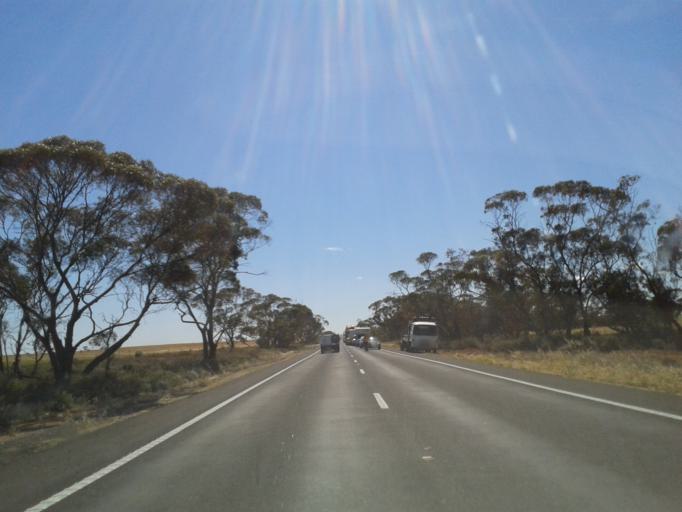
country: AU
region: New South Wales
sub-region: Wentworth
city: Dareton
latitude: -34.2704
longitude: 141.8001
